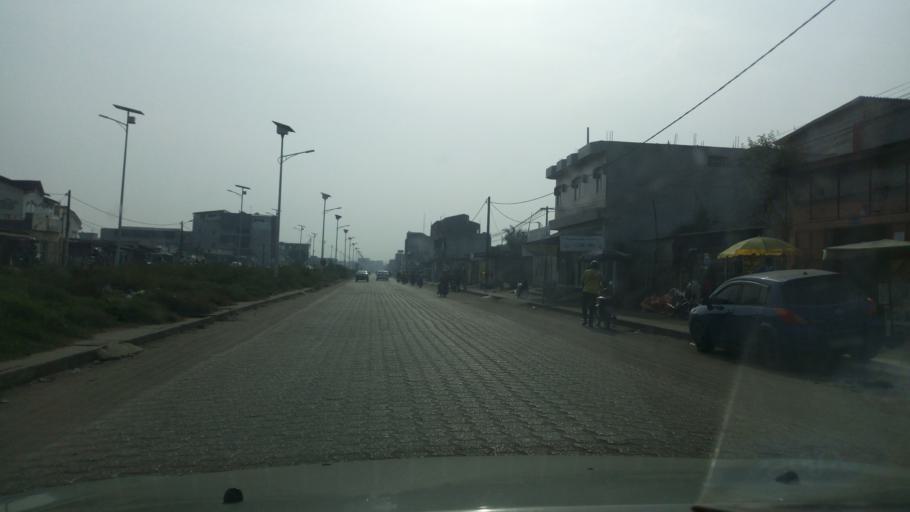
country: BJ
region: Littoral
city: Cotonou
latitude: 6.3745
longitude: 2.3509
